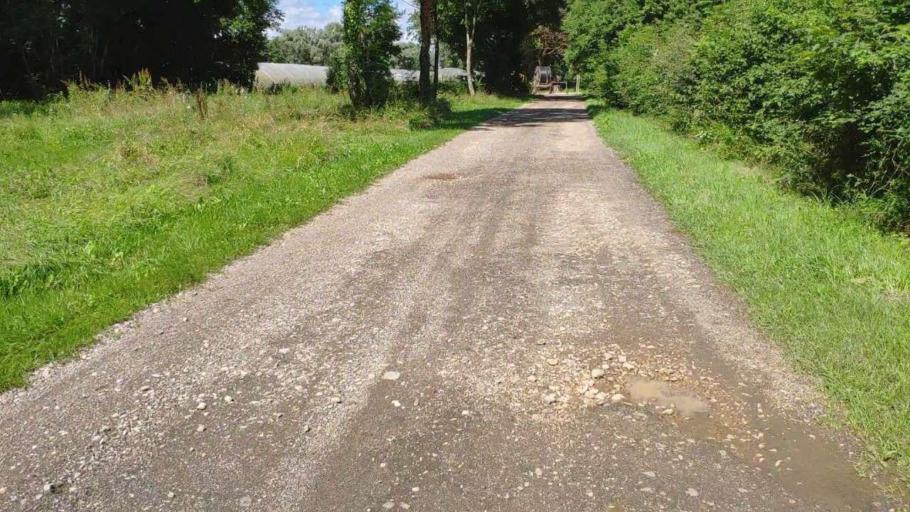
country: FR
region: Franche-Comte
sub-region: Departement du Jura
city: Bletterans
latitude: 46.8271
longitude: 5.5554
